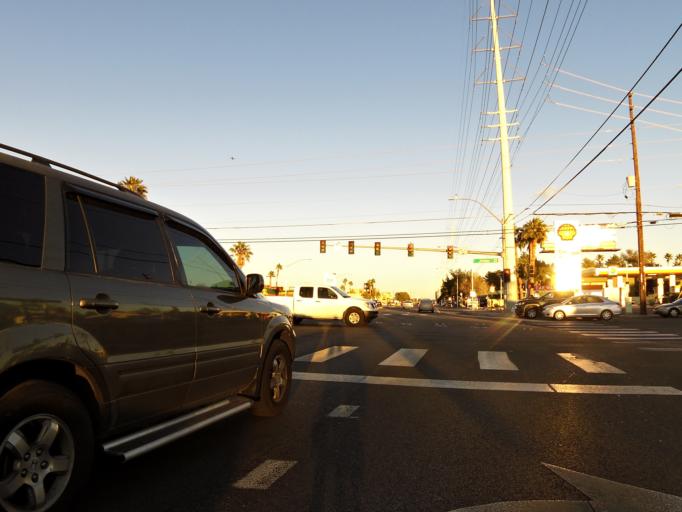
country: US
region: Nevada
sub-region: Clark County
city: Spring Valley
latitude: 36.1144
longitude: -115.2252
